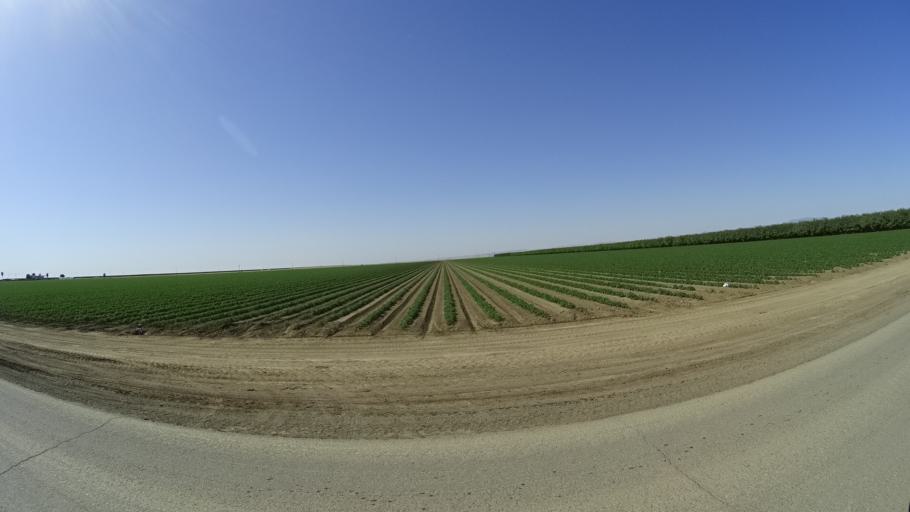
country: US
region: California
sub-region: Kings County
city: Lemoore Station
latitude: 36.1815
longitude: -119.9668
